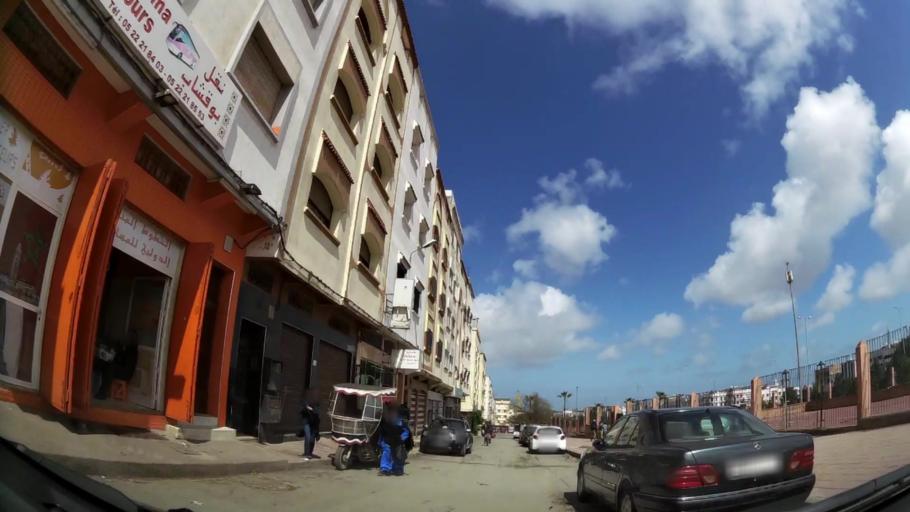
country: MA
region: Grand Casablanca
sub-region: Casablanca
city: Casablanca
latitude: 33.5401
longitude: -7.5796
